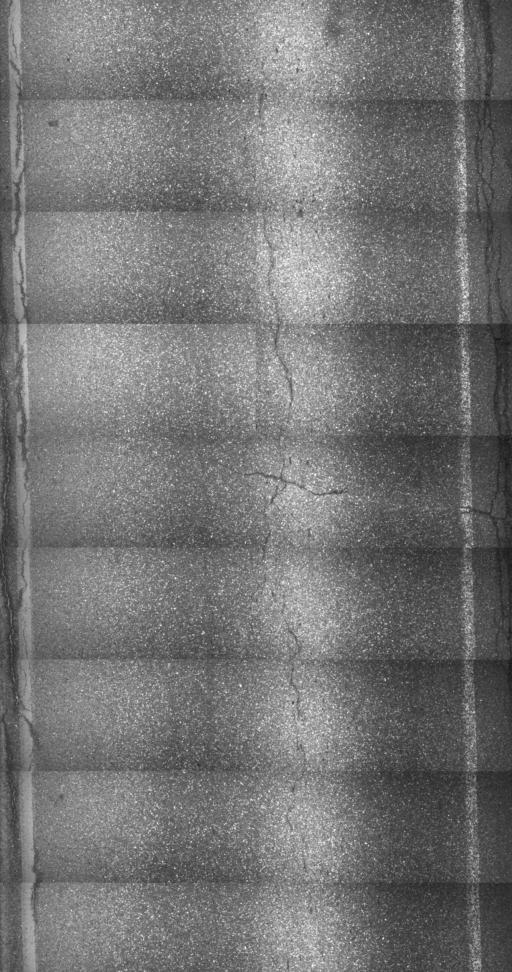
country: US
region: Vermont
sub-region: Lamoille County
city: Johnson
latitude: 44.6471
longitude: -72.8666
